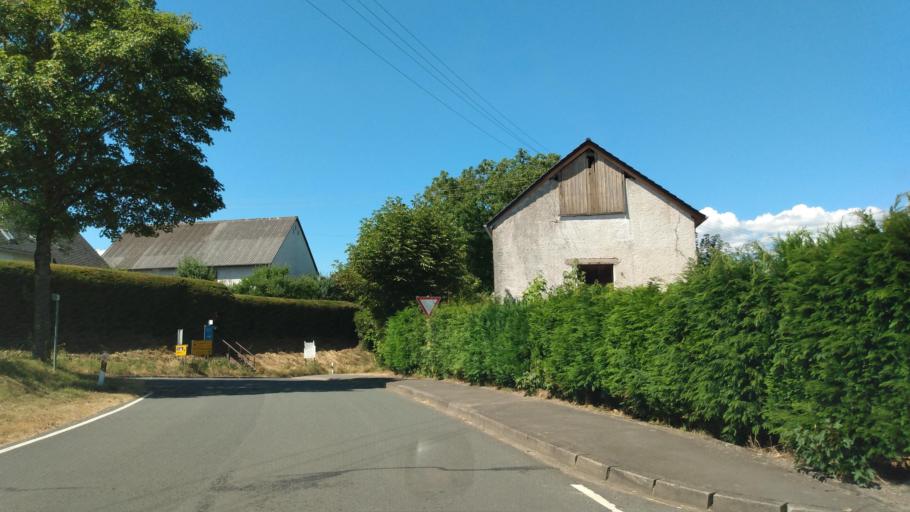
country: DE
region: Rheinland-Pfalz
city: Oberkail
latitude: 50.0346
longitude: 6.6794
